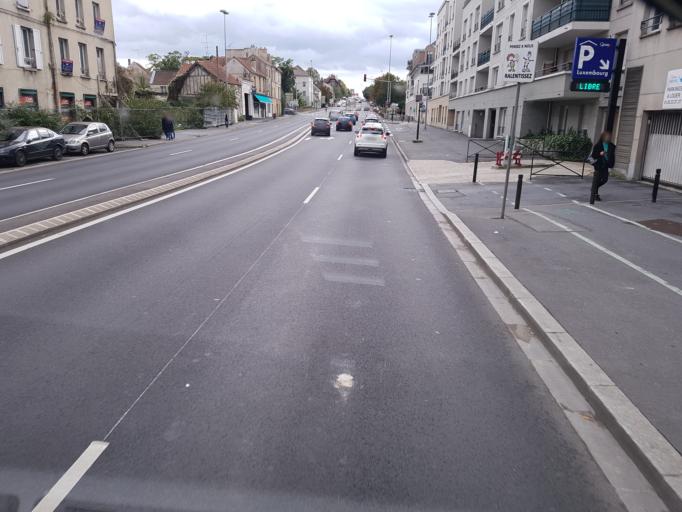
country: FR
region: Ile-de-France
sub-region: Departement de Seine-et-Marne
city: Meaux
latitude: 48.9541
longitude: 2.8793
